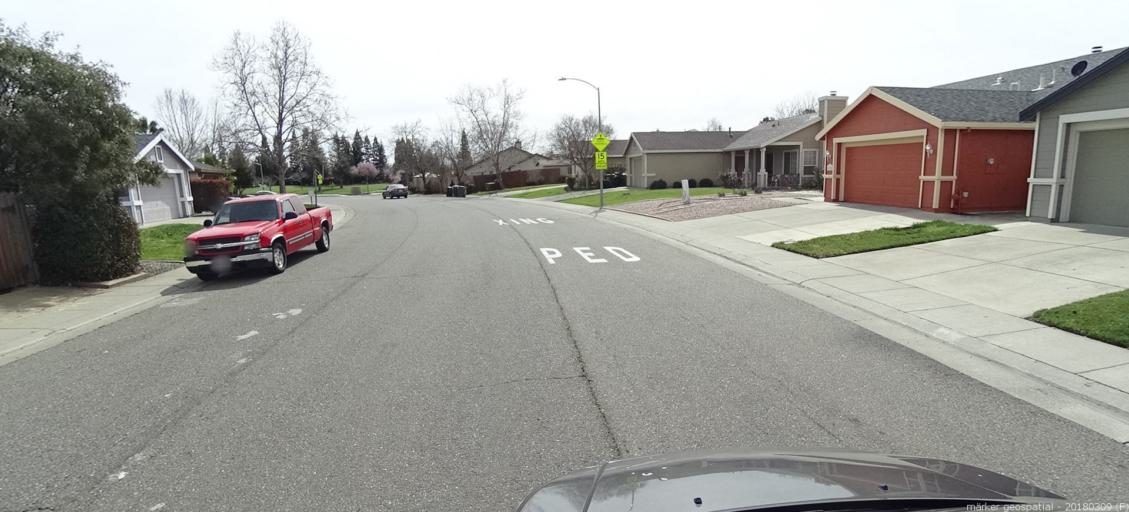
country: US
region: California
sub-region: Sacramento County
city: Vineyard
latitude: 38.4553
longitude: -121.3620
